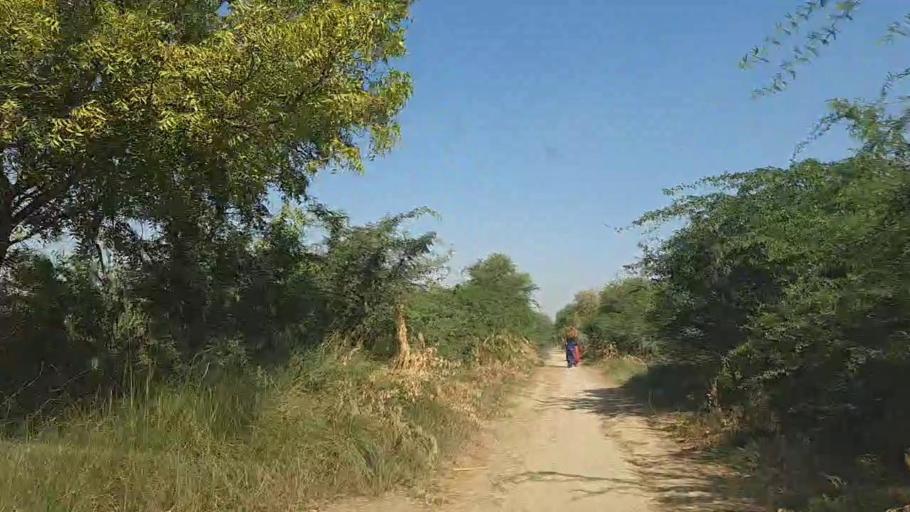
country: PK
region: Sindh
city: Thatta
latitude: 24.7849
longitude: 67.9734
